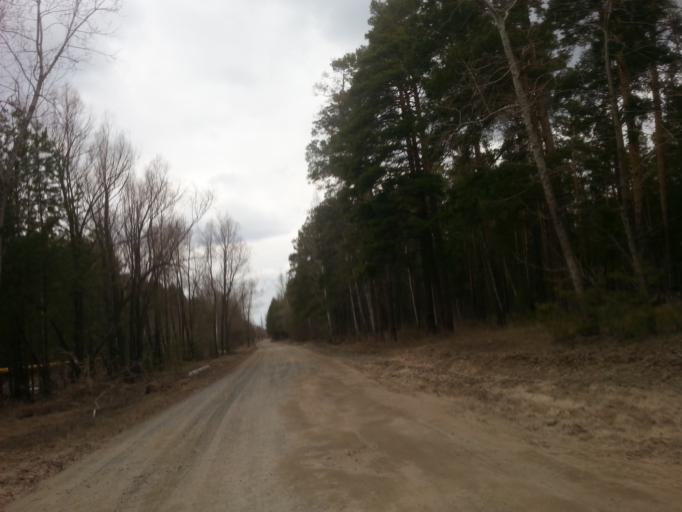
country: RU
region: Altai Krai
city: Yuzhnyy
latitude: 53.2804
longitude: 83.7348
